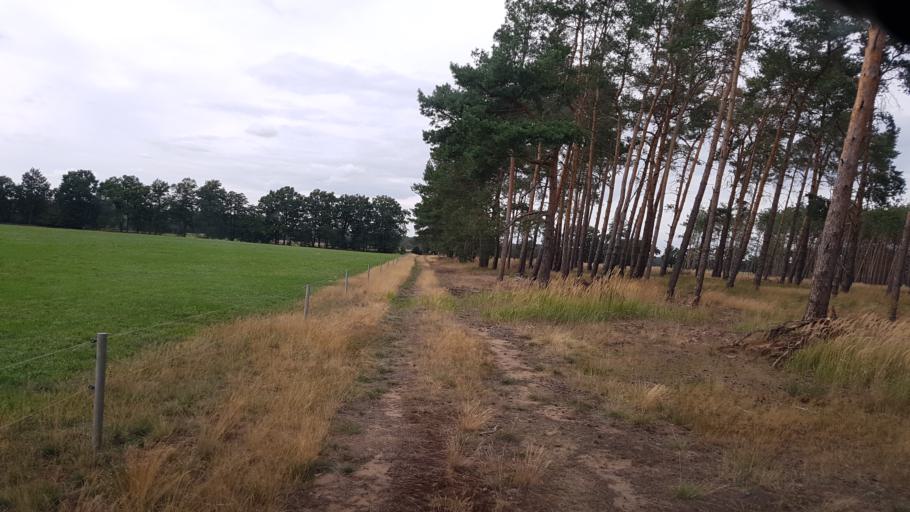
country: DE
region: Brandenburg
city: Bad Liebenwerda
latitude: 51.5482
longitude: 13.3463
